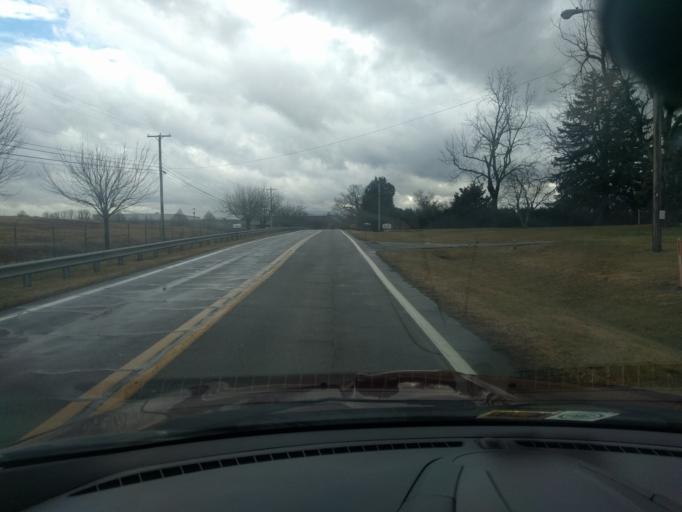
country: US
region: Virginia
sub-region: Roanoke County
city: Hollins
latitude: 37.3176
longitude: -79.9798
